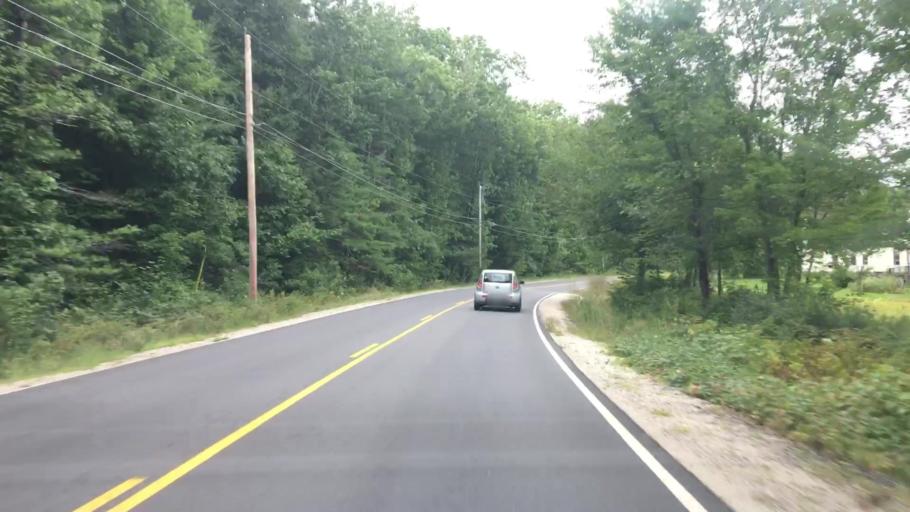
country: US
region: Maine
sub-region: Cumberland County
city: New Gloucester
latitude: 43.8872
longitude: -70.2526
